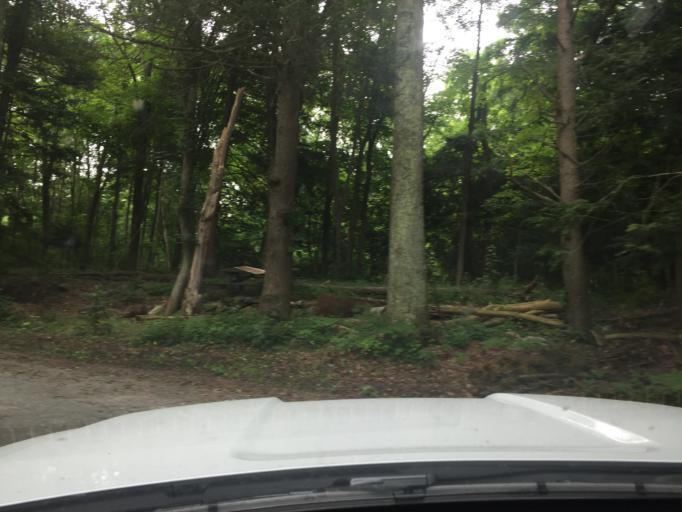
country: US
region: Connecticut
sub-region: New London County
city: Montville Center
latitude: 41.5733
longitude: -72.2048
